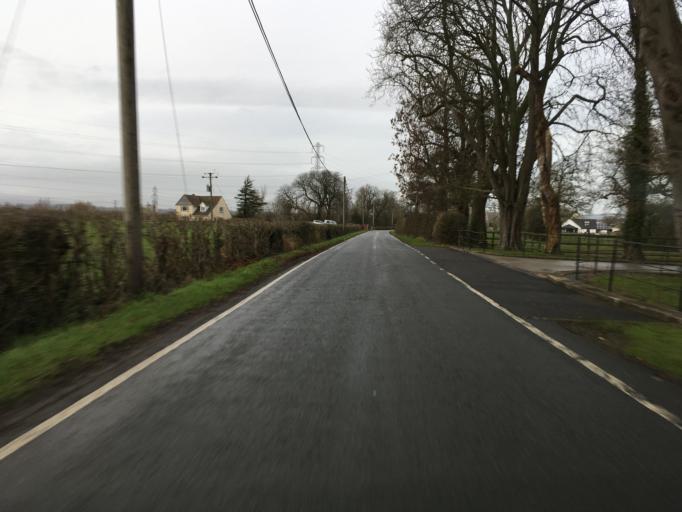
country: GB
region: Wales
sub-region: Newport
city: Goldcliff
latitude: 51.5580
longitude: -2.9099
